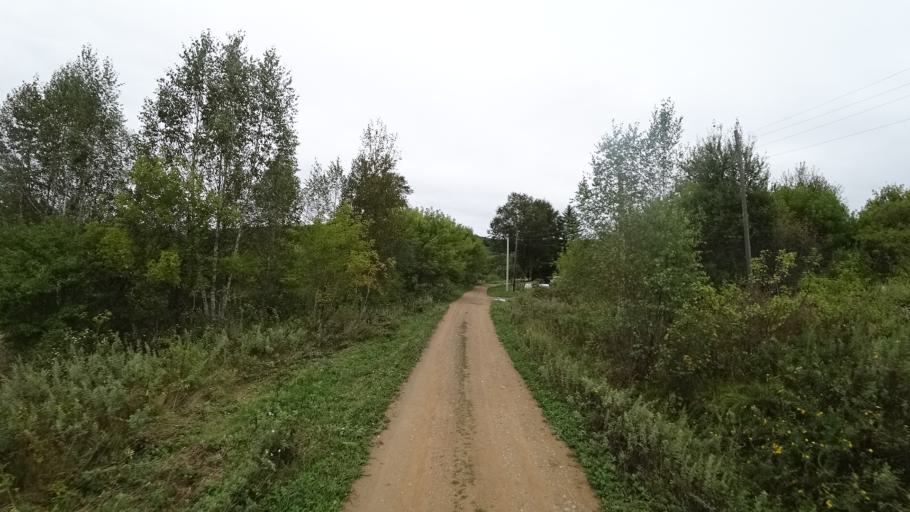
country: RU
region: Primorskiy
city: Rettikhovka
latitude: 44.1747
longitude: 132.8859
